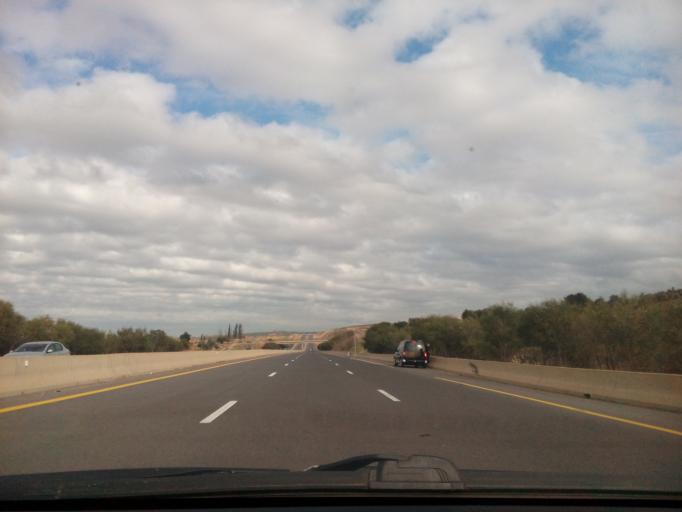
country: DZ
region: Tlemcen
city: Chetouane
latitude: 34.9480
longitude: -1.3057
